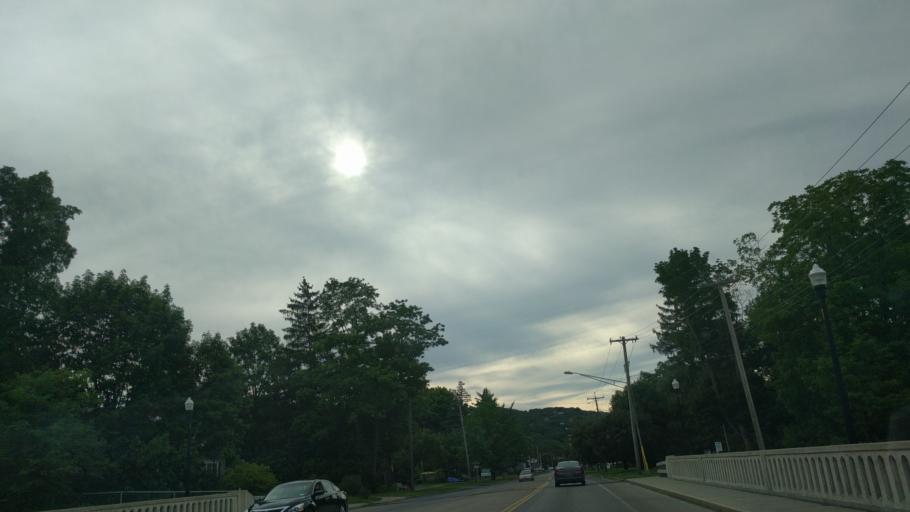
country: US
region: New York
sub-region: Onondaga County
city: Nedrow
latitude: 43.0015
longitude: -76.1485
